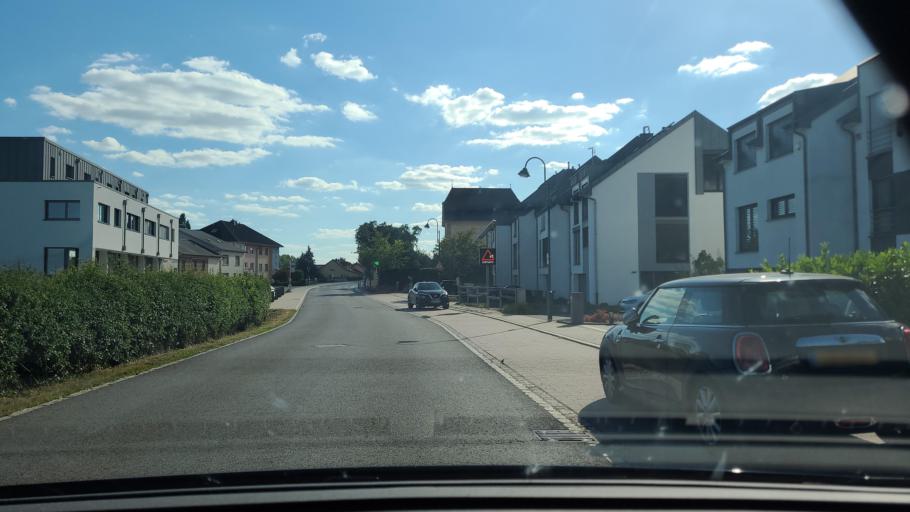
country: LU
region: Luxembourg
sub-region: Canton de Capellen
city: Mamer
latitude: 49.6184
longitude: 5.9997
